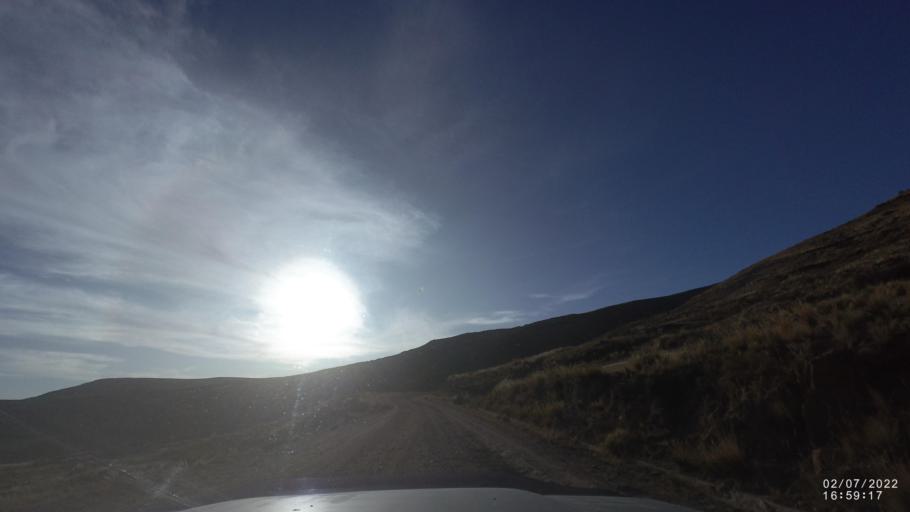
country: BO
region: Cochabamba
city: Irpa Irpa
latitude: -17.9411
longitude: -66.5501
